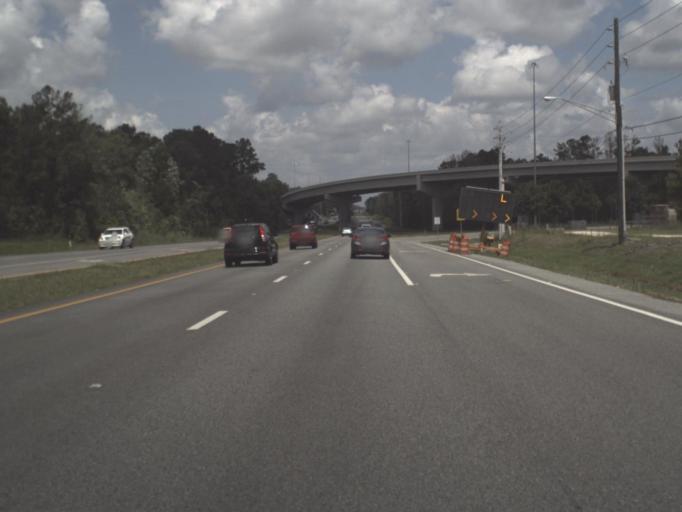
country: US
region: Florida
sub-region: Saint Johns County
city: Palm Valley
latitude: 30.0953
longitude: -81.4692
